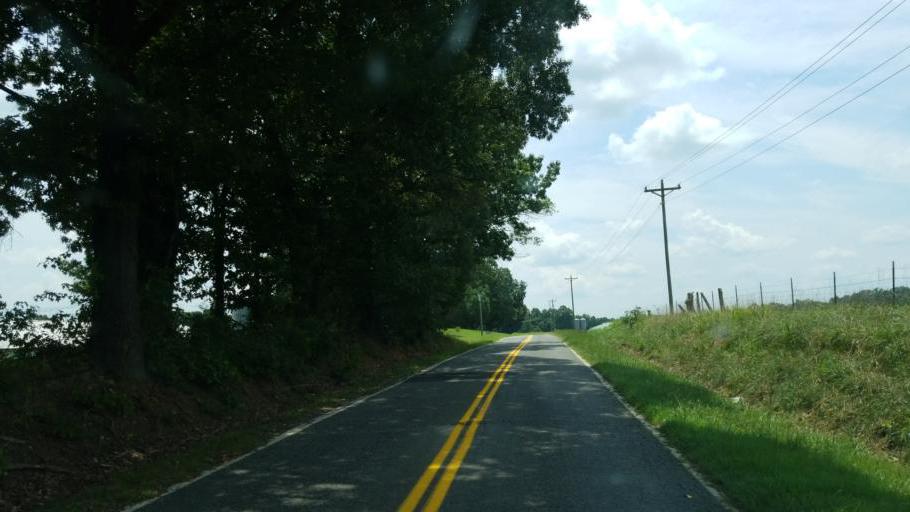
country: US
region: South Carolina
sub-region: Cherokee County
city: Blacksburg
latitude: 35.0828
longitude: -81.4007
